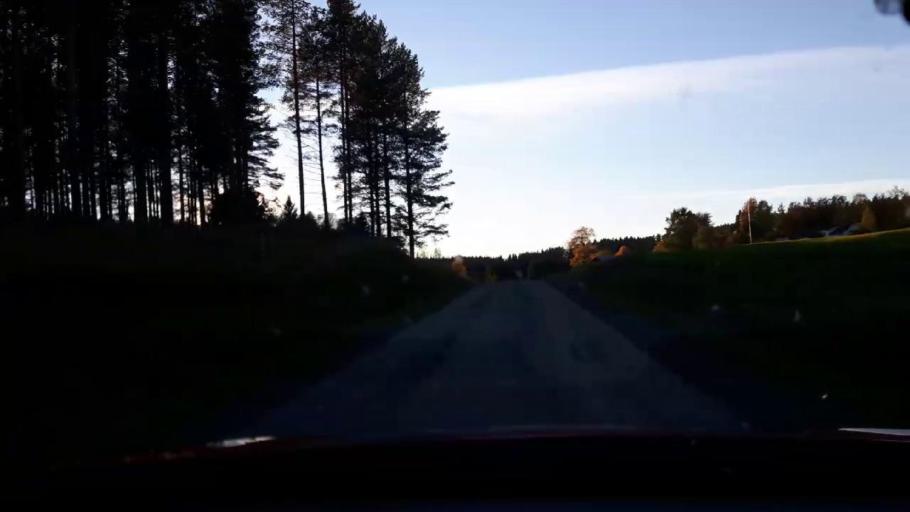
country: SE
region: Jaemtland
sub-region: Krokoms Kommun
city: Krokom
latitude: 63.4820
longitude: 14.3188
